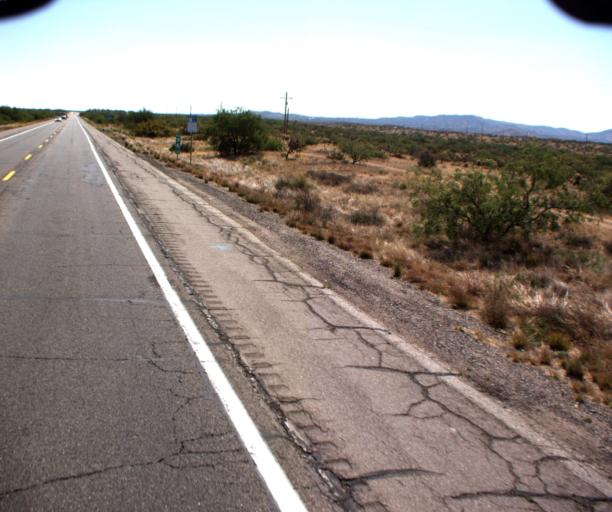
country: US
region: Arizona
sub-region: Pinal County
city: Oracle
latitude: 32.6007
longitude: -110.8712
